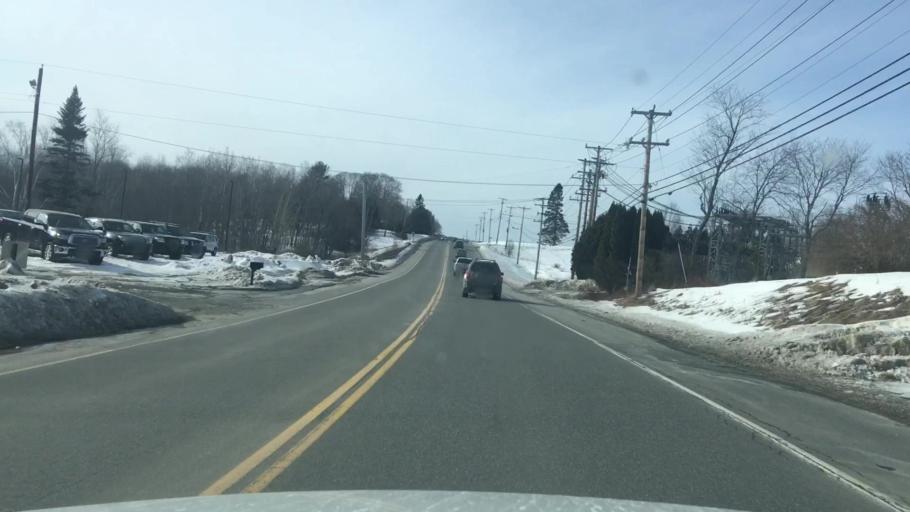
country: US
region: Maine
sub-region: Penobscot County
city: Bangor
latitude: 44.8523
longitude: -68.8078
